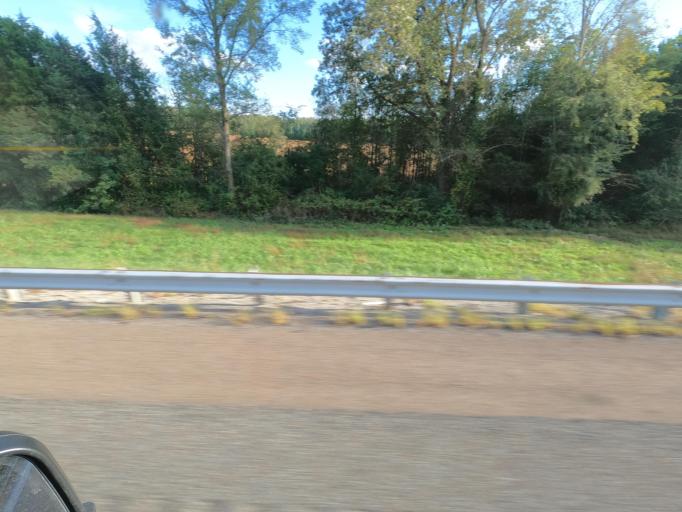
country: US
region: Tennessee
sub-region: Henderson County
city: Lexington
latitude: 35.7830
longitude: -88.4105
